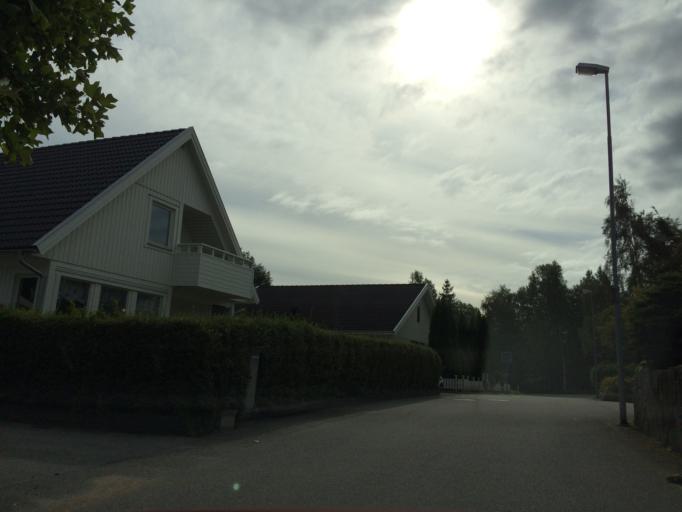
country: SE
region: Vaestra Goetaland
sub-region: Trollhattan
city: Trollhattan
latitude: 58.3209
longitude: 12.2774
